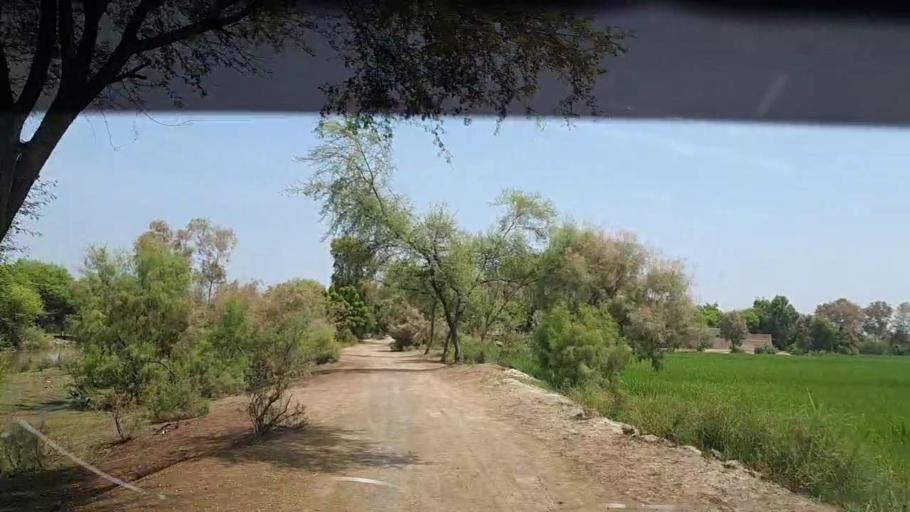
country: PK
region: Sindh
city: Tangwani
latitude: 28.2268
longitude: 68.9108
